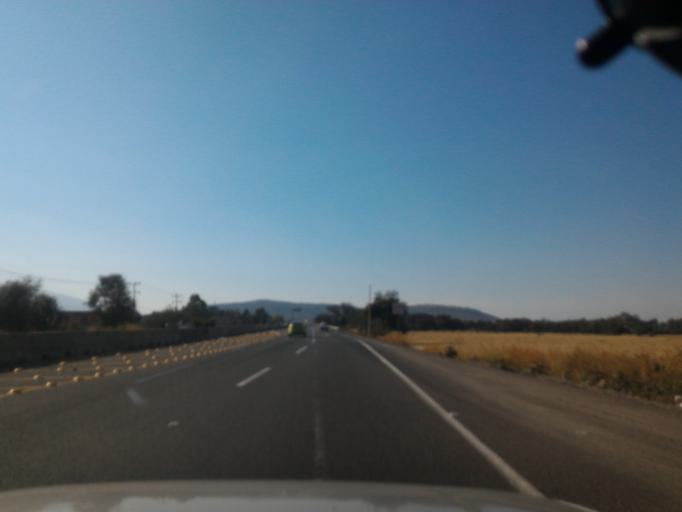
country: MX
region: Jalisco
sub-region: Ixtlahuacan de los Membrillos
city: Valle de los Girasoles [Fraccionamiento]
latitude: 20.4117
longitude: -103.2159
